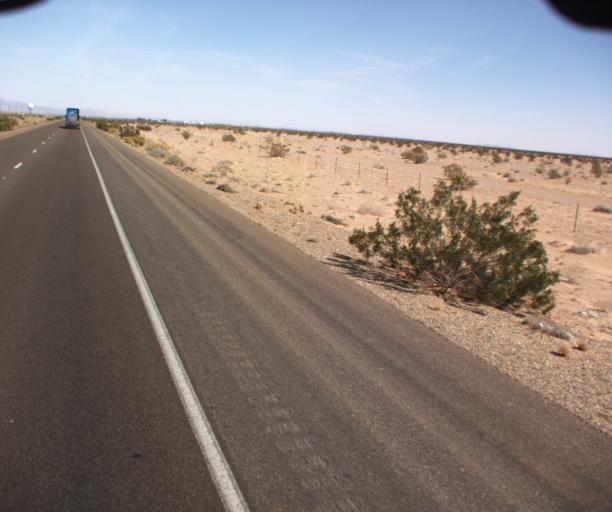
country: MX
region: Sonora
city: San Luis Rio Colorado
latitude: 32.4945
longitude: -114.6723
